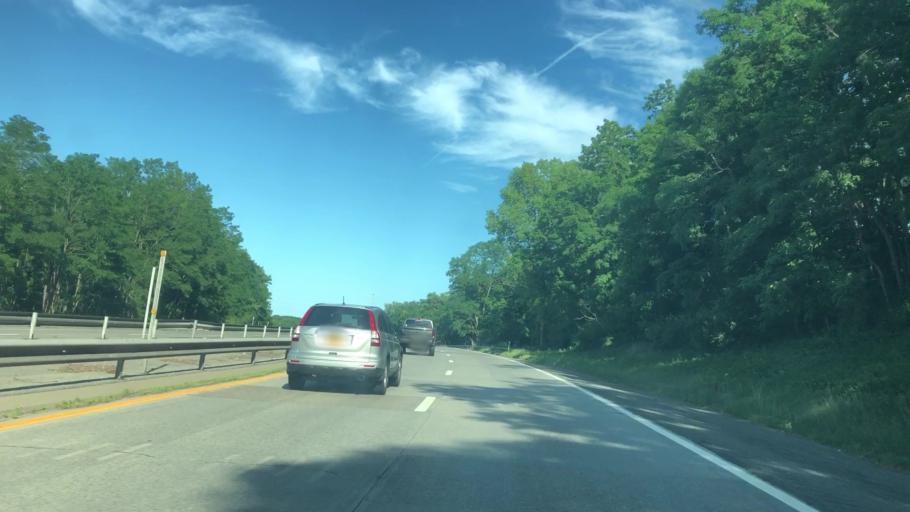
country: US
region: New York
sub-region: Monroe County
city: East Rochester
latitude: 43.1235
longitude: -77.5155
